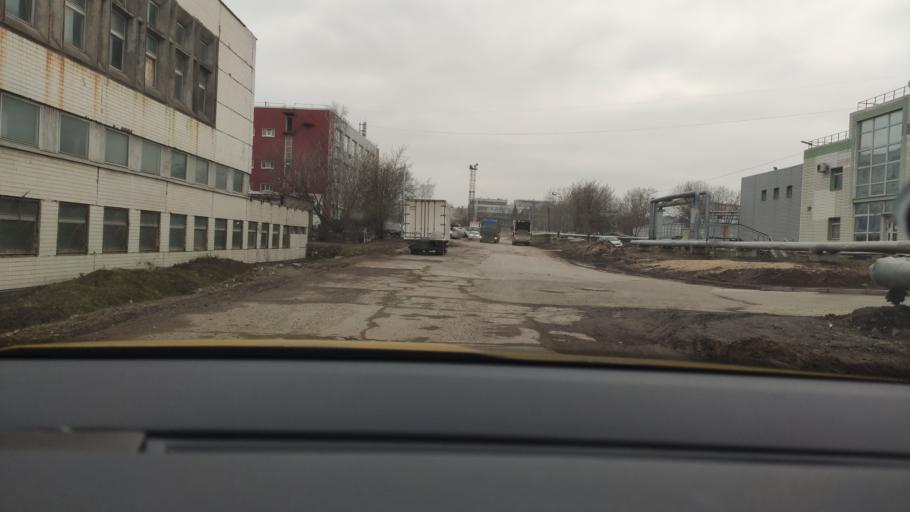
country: RU
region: Moscow
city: Tsaritsyno
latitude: 55.6094
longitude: 37.6329
